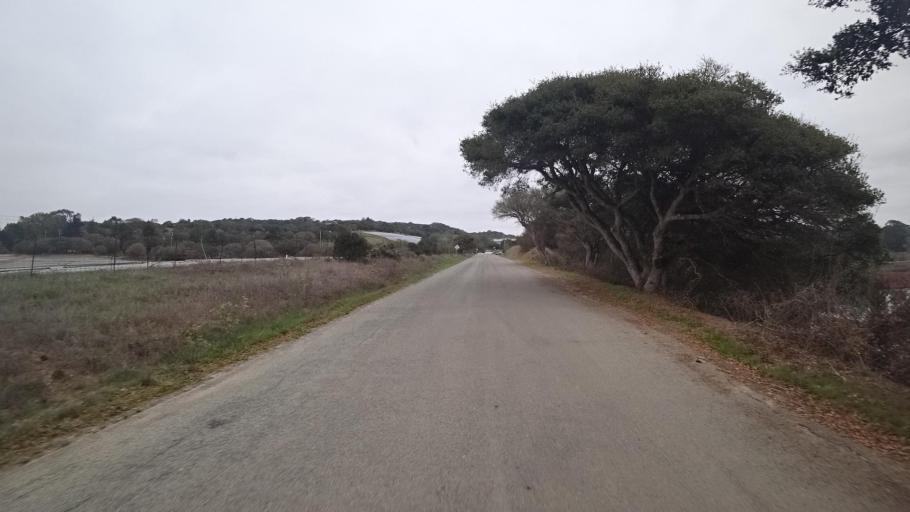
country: US
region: California
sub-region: Monterey County
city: Elkhorn
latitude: 36.8419
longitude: -121.7442
